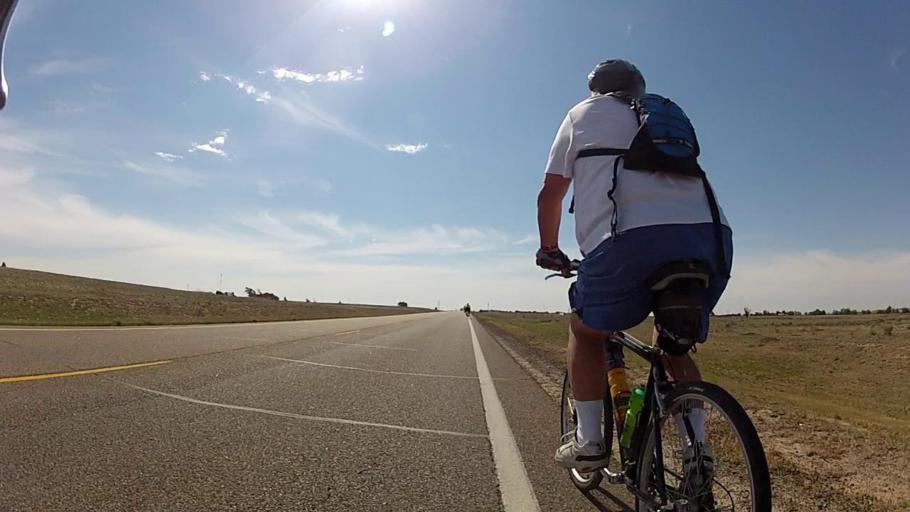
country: US
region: Kansas
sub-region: Grant County
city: Ulysses
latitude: 37.5678
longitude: -101.3216
